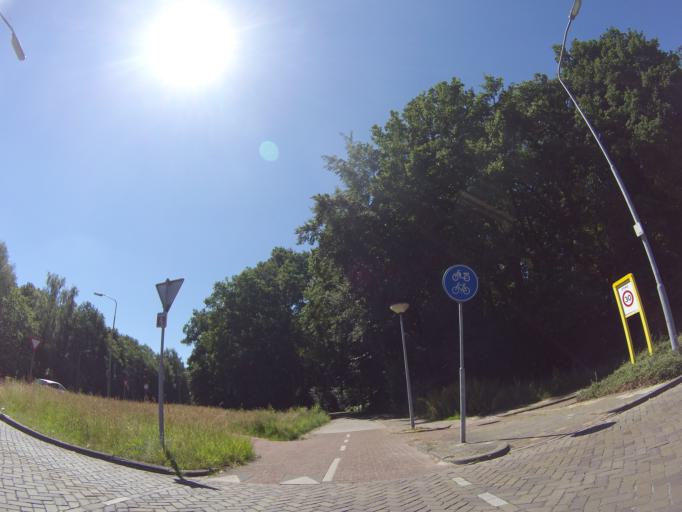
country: NL
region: Drenthe
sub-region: Gemeente Assen
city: Assen
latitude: 52.9866
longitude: 6.5679
